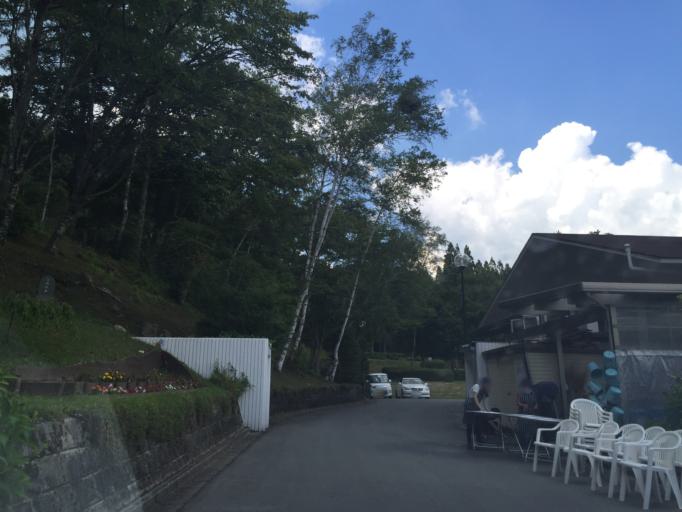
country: JP
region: Nagano
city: Iida
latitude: 35.4022
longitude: 137.6860
